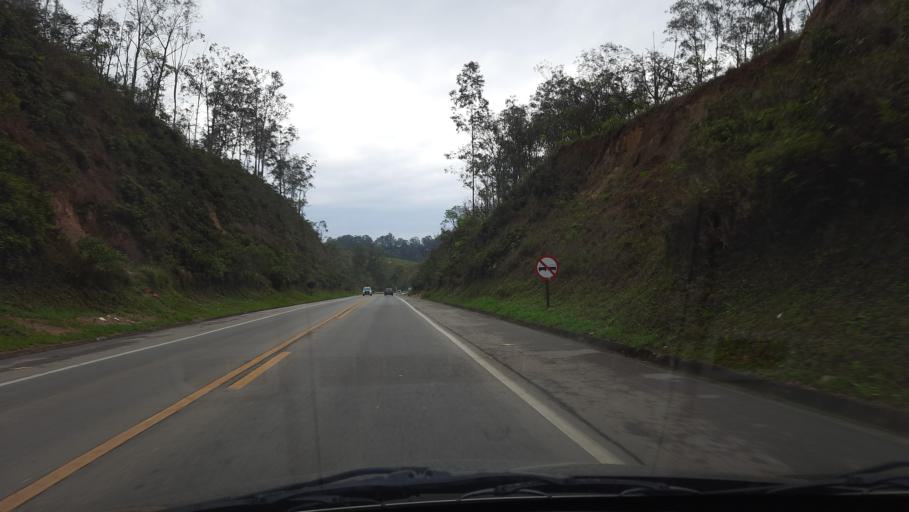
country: BR
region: Sao Paulo
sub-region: Franco Da Rocha
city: Franco da Rocha
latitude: -23.3339
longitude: -46.6700
